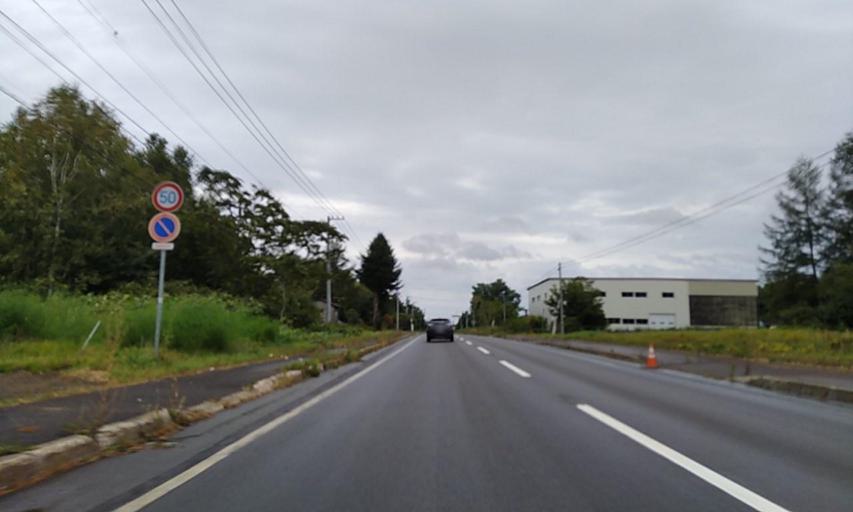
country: JP
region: Hokkaido
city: Kitami
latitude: 44.0831
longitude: 143.9471
